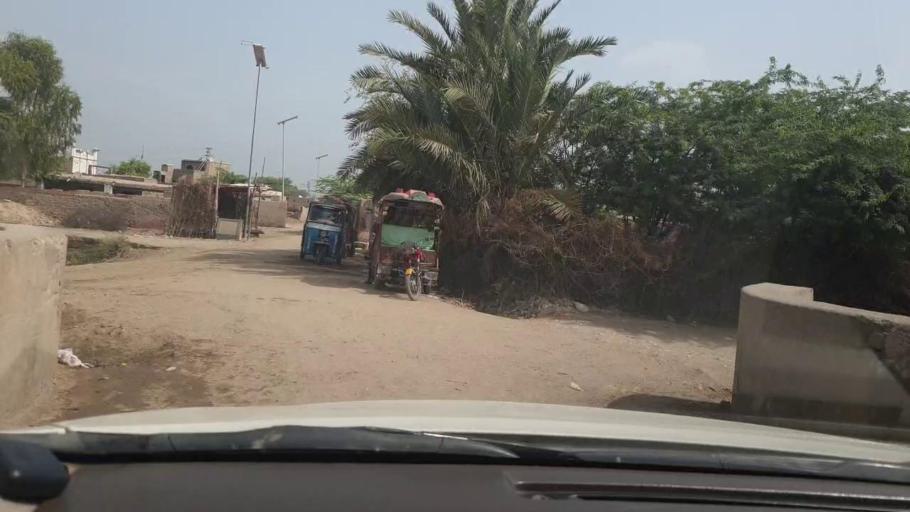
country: PK
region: Sindh
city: Shikarpur
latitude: 28.0057
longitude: 68.5931
